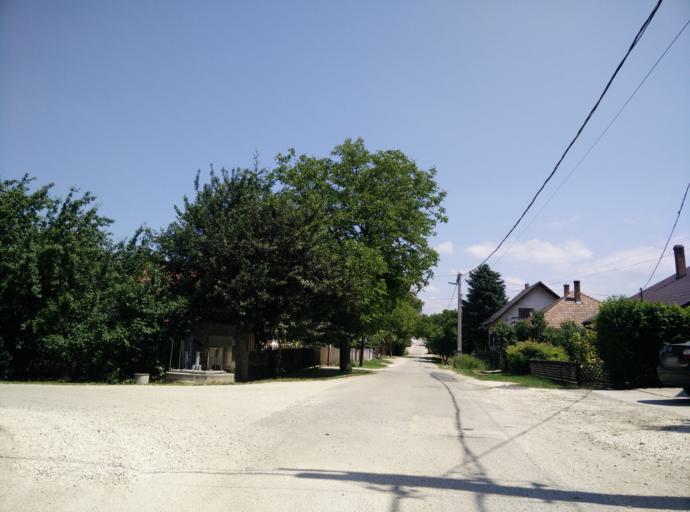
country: HU
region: Pest
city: Biatorbagy
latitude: 47.4669
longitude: 18.8218
